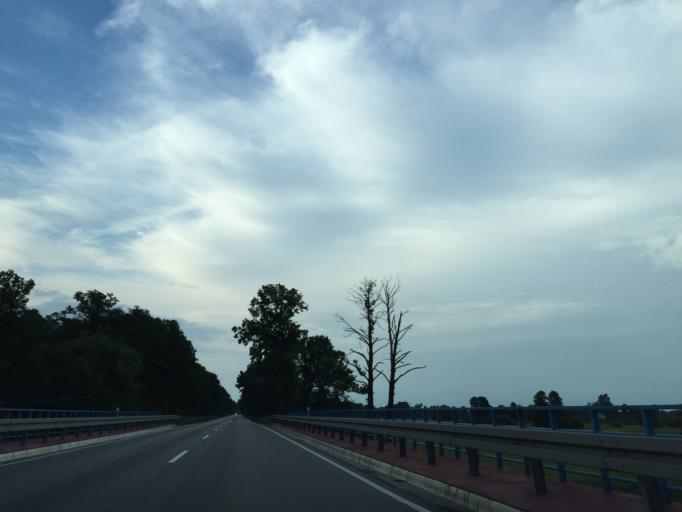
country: PL
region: Masovian Voivodeship
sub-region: Powiat wegrowski
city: Sadowne
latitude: 52.6487
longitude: 21.8464
